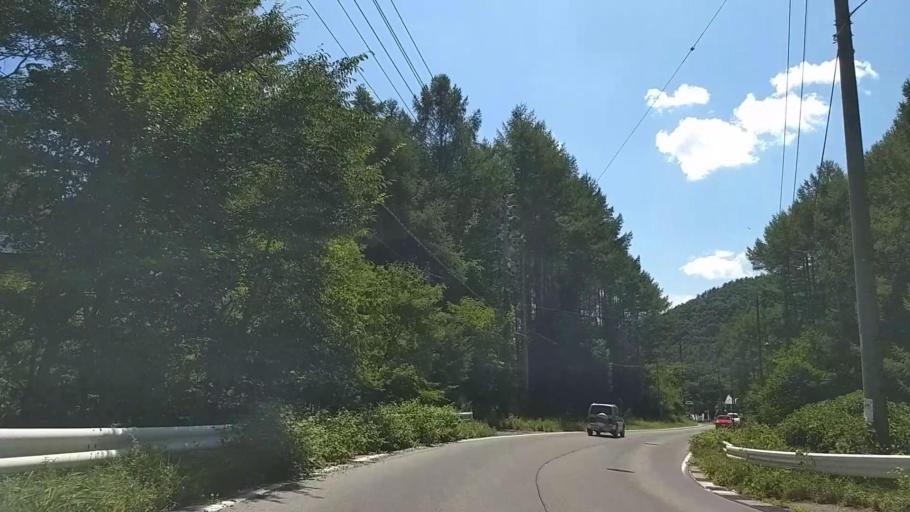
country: JP
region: Nagano
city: Chino
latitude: 36.0677
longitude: 138.2234
